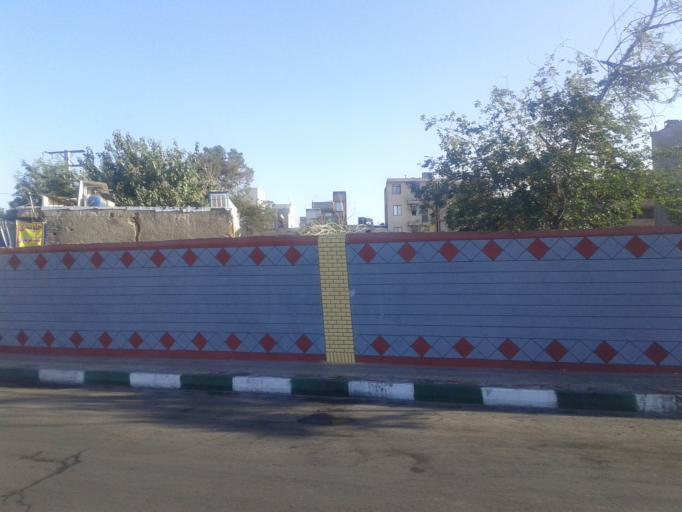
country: IR
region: Tehran
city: Rey
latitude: 35.6258
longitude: 51.3570
